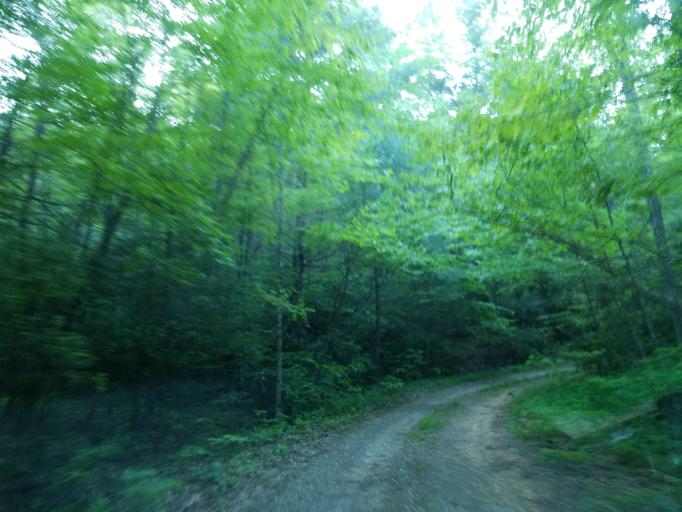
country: US
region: Georgia
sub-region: Lumpkin County
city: Dahlonega
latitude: 34.6666
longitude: -84.1310
